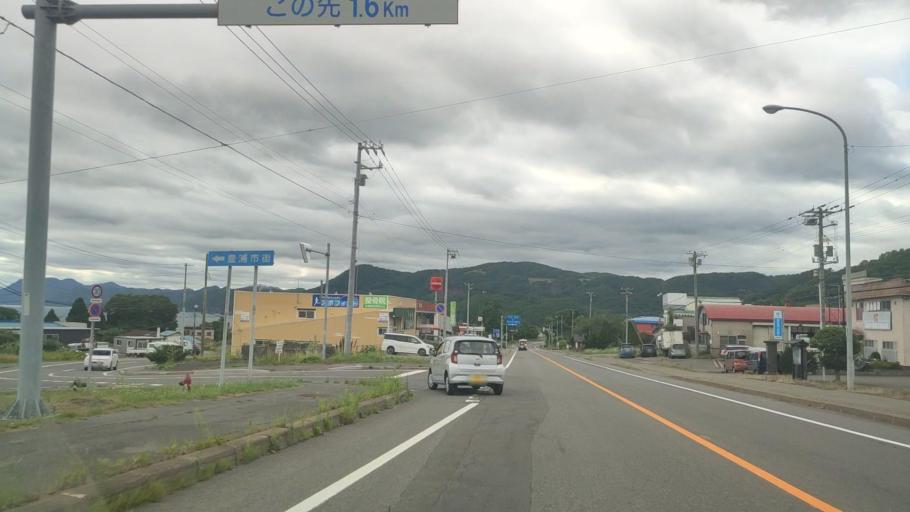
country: JP
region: Hokkaido
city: Date
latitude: 42.5815
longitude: 140.7169
